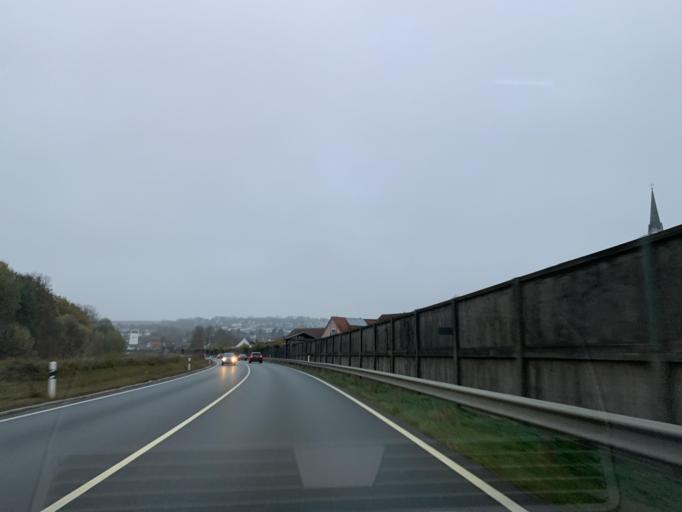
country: DE
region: Bavaria
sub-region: Lower Bavaria
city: Bad Abbach
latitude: 48.9339
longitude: 12.0374
